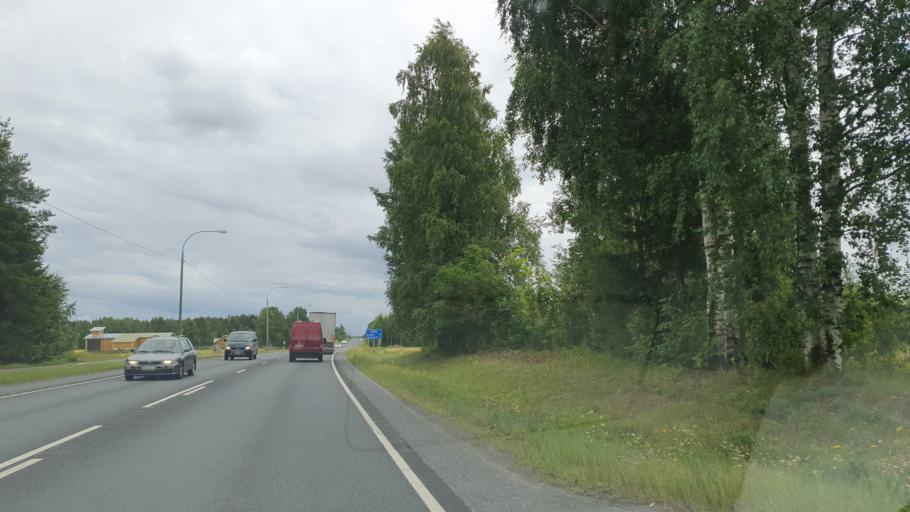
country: FI
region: Northern Savo
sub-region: Ylae-Savo
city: Lapinlahti
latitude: 63.4549
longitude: 27.3168
